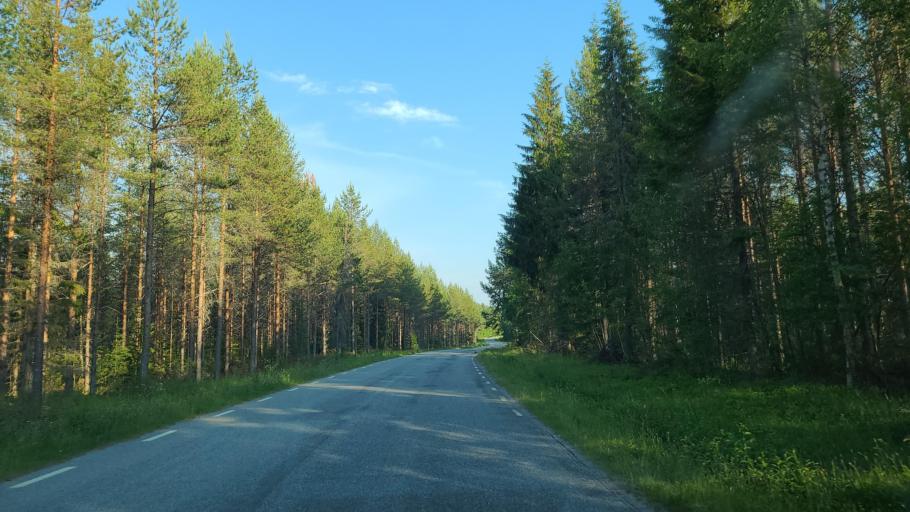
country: SE
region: Vaesterbotten
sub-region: Skelleftea Kommun
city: Burea
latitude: 64.3616
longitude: 21.3335
